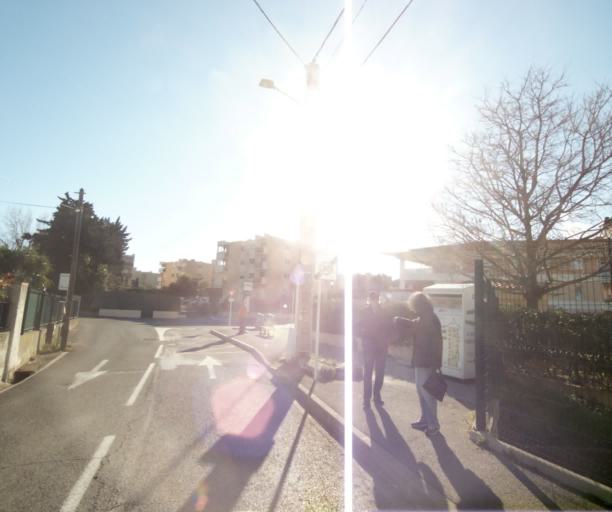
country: FR
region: Provence-Alpes-Cote d'Azur
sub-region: Departement des Alpes-Maritimes
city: Antibes
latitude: 43.5947
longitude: 7.1229
